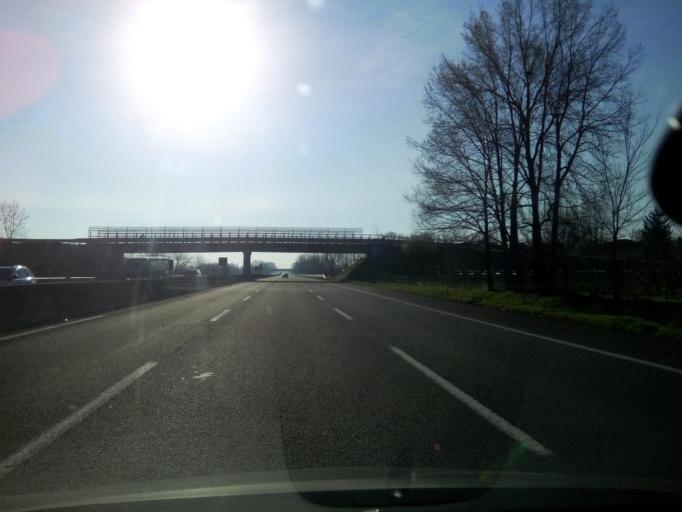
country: IT
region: Emilia-Romagna
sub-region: Provincia di Modena
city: Campogalliano
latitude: 44.6735
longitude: 10.8273
